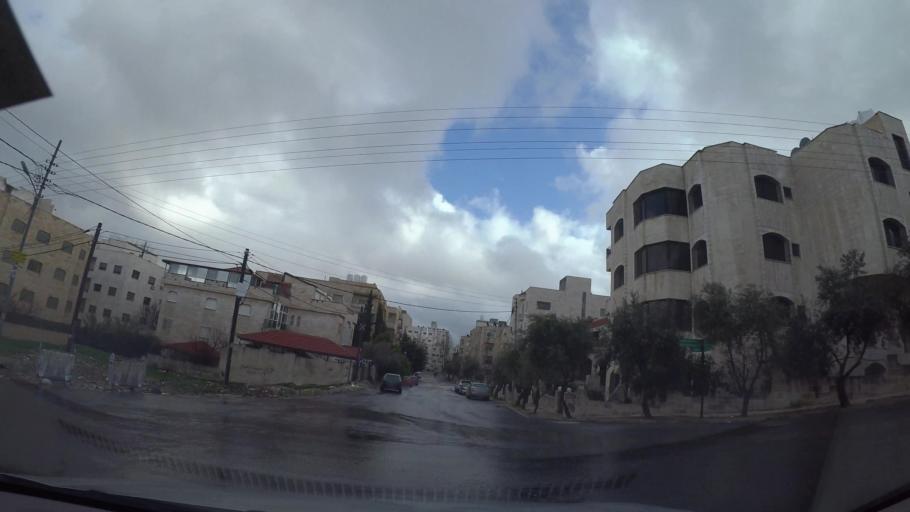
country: JO
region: Amman
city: Al Jubayhah
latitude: 32.0314
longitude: 35.8696
